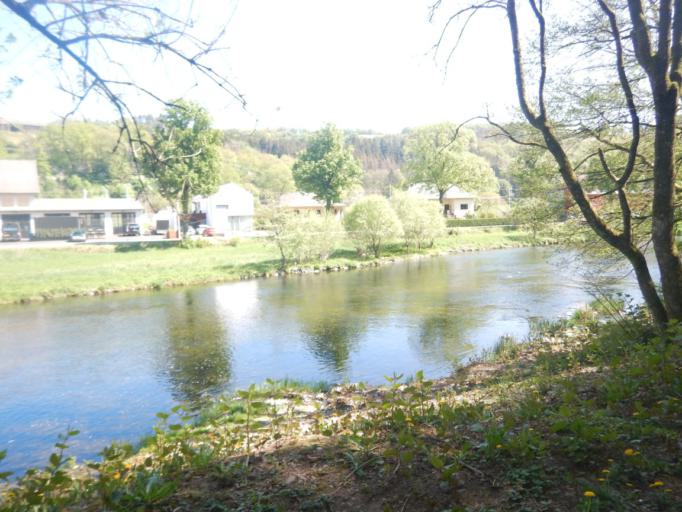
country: LU
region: Diekirch
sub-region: Canton de Diekirch
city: Bourscheid
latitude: 49.8953
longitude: 6.0910
